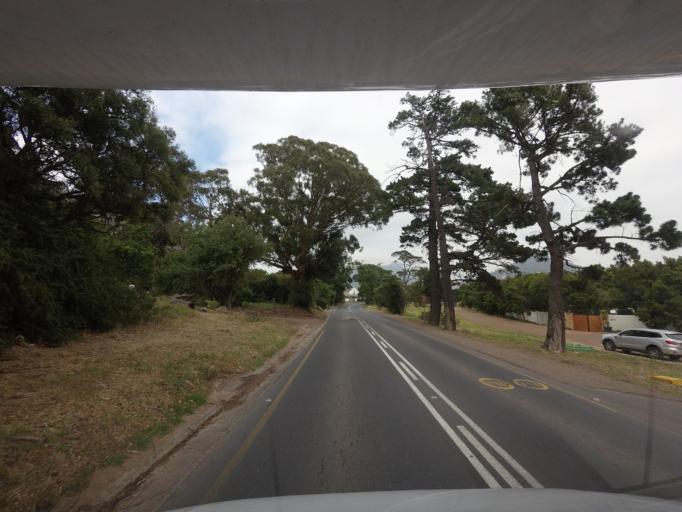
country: ZA
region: Western Cape
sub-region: City of Cape Town
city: Constantia
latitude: -34.0185
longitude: 18.3777
